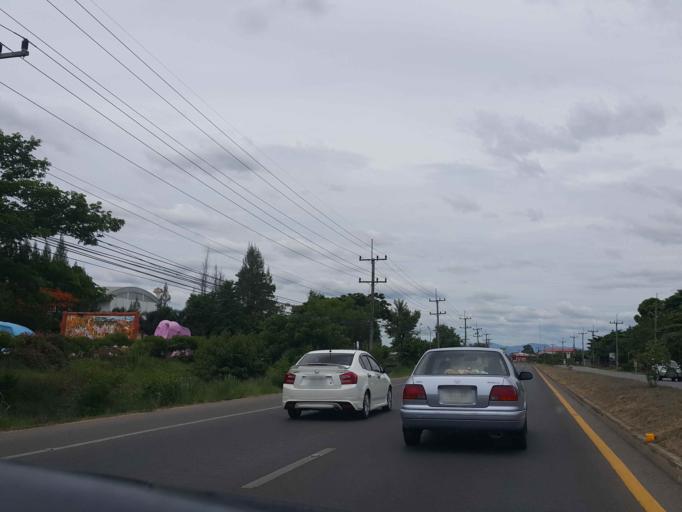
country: TH
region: Lamphun
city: Pa Sang
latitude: 18.5483
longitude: 98.8659
